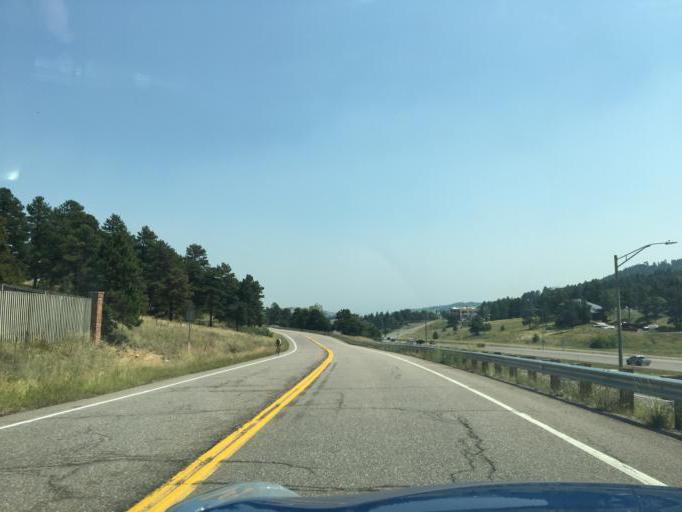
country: US
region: Colorado
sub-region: Jefferson County
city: Genesee
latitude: 39.7100
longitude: -105.2917
